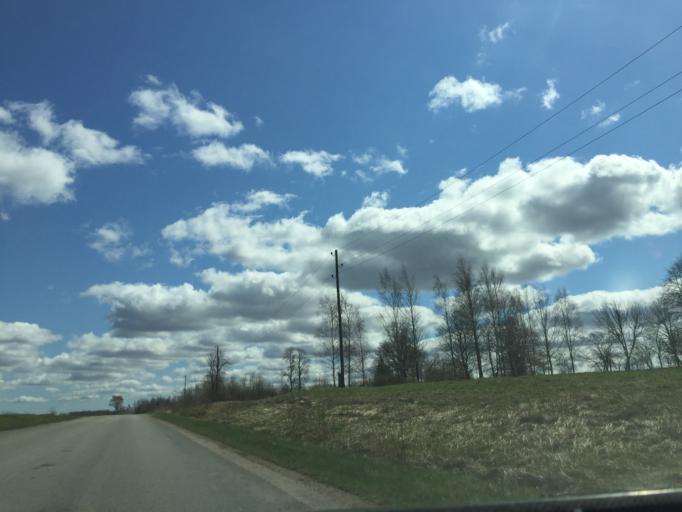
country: LV
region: Vilanu
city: Vilani
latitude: 56.7227
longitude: 27.0899
